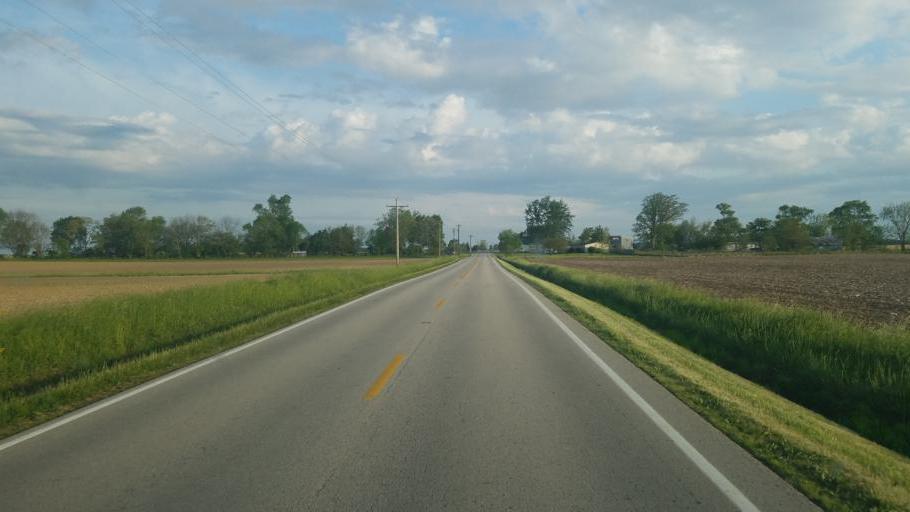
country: US
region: Ohio
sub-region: Highland County
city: Leesburg
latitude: 39.4079
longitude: -83.6072
